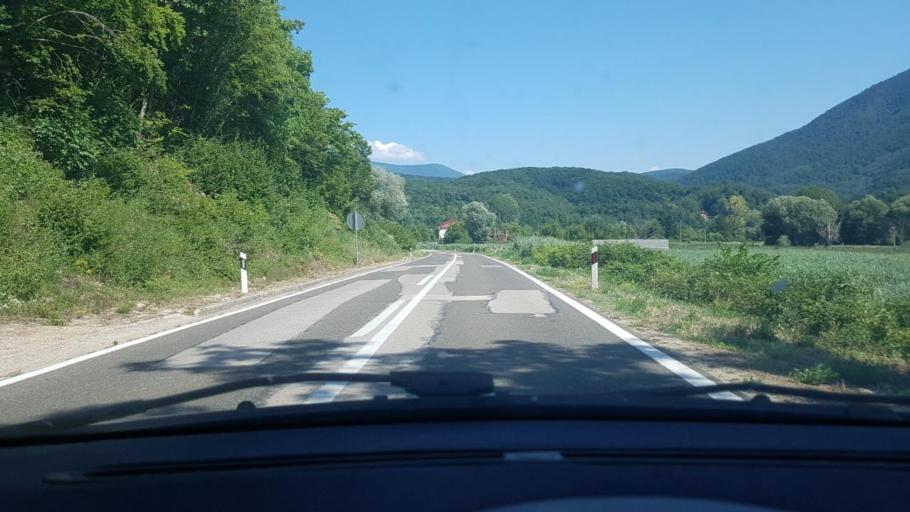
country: BA
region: Federation of Bosnia and Herzegovina
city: Bihac
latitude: 44.7514
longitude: 15.9353
